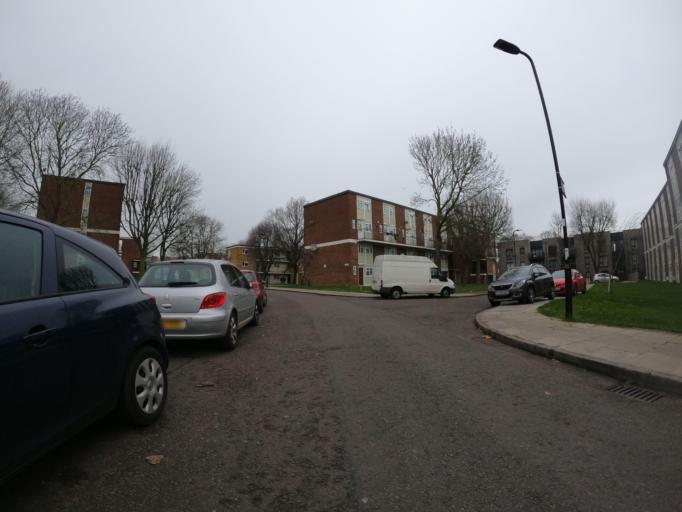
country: GB
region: England
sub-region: Greater London
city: Greenford
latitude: 51.5188
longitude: -0.3631
